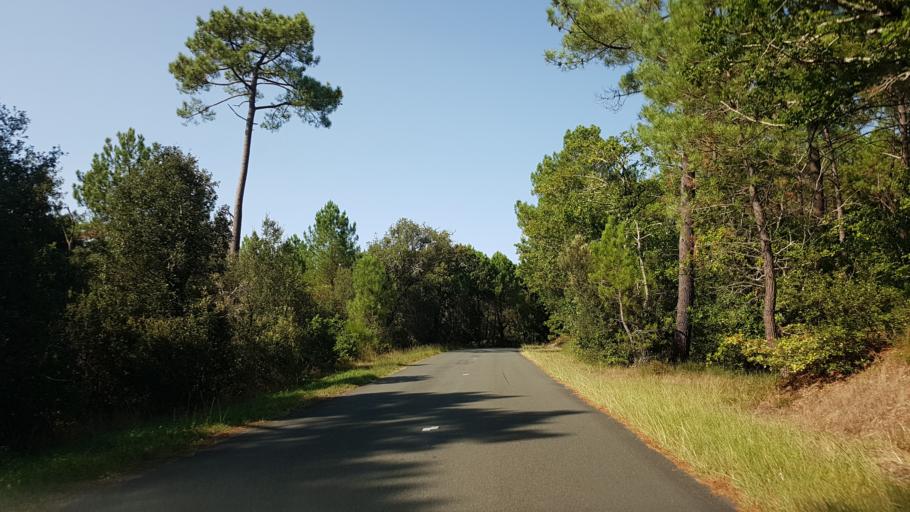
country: FR
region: Poitou-Charentes
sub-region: Departement de la Charente-Maritime
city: Saint-Palais-sur-Mer
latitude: 45.6678
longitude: -1.1235
